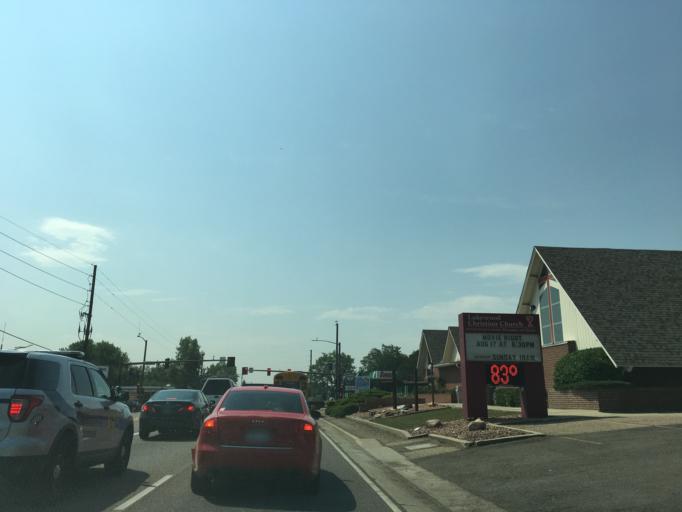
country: US
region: Colorado
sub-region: Jefferson County
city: Wheat Ridge
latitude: 39.7484
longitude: -105.1097
